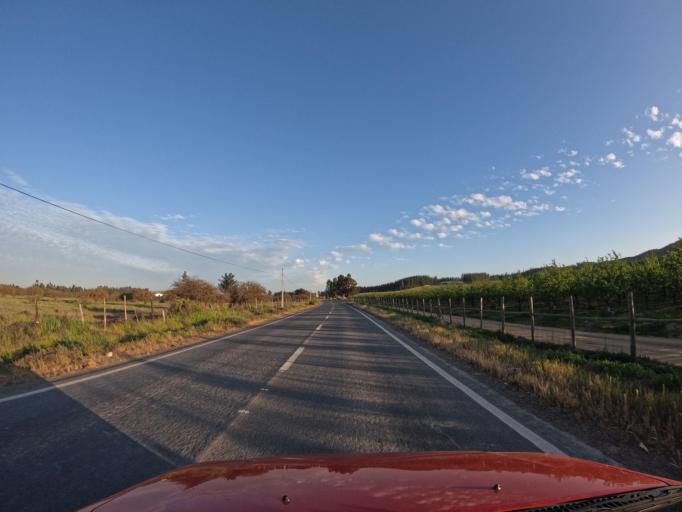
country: CL
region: O'Higgins
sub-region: Provincia de Colchagua
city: Santa Cruz
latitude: -34.3375
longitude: -71.7442
